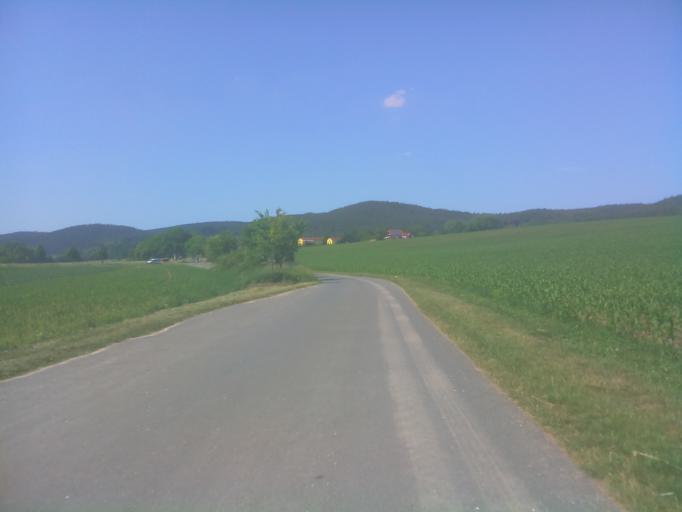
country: DE
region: Thuringia
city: Possneck
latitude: 50.7167
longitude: 11.6124
